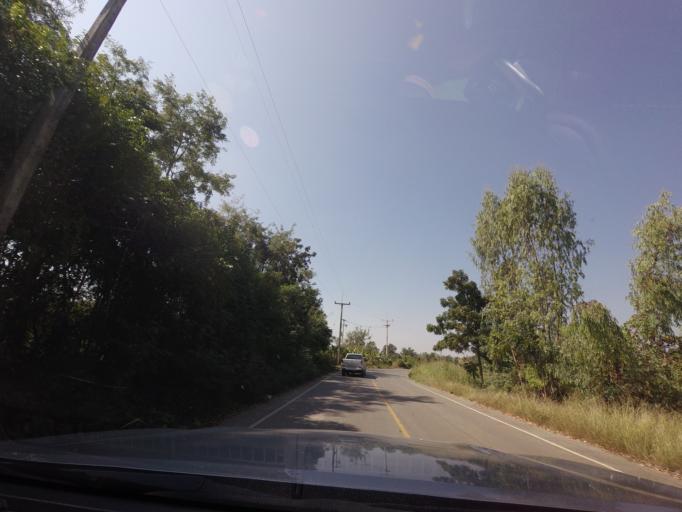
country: TH
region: Sukhothai
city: Si Samrong
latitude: 17.1308
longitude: 99.7801
